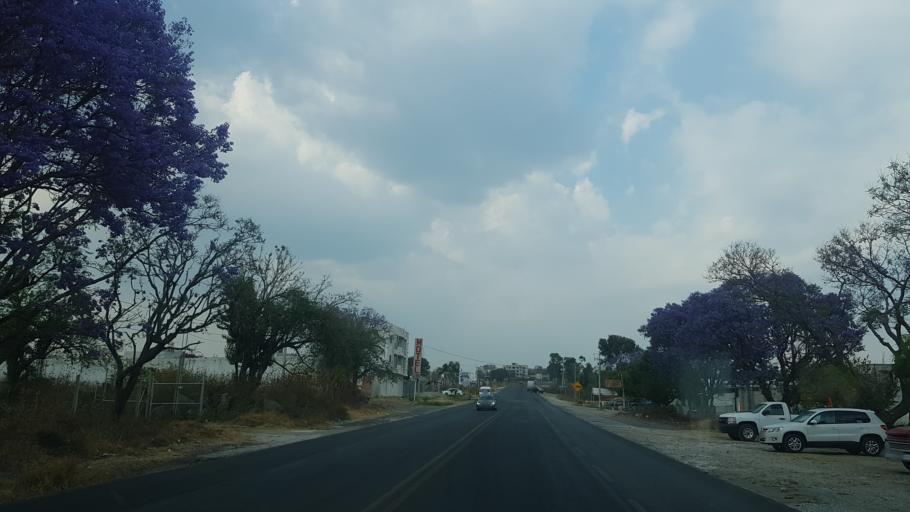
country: MX
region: Puebla
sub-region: Santa Isabel Cholula
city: Santa Ana Acozautla
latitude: 18.9611
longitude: -98.3859
